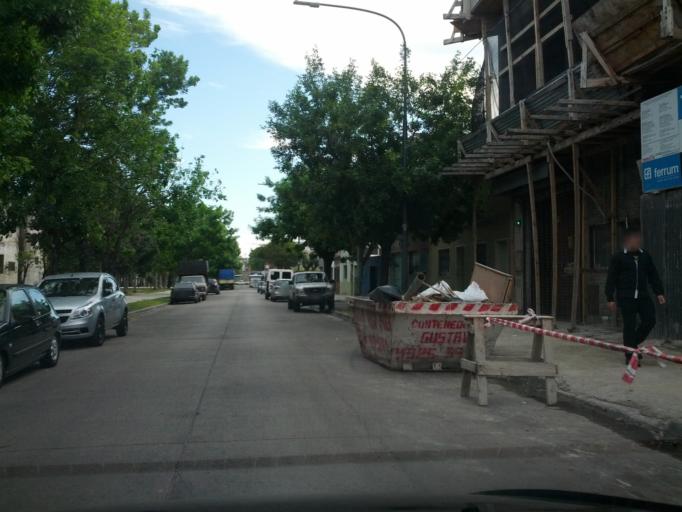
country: AR
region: Buenos Aires F.D.
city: Villa Lugano
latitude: -34.6517
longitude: -58.4283
